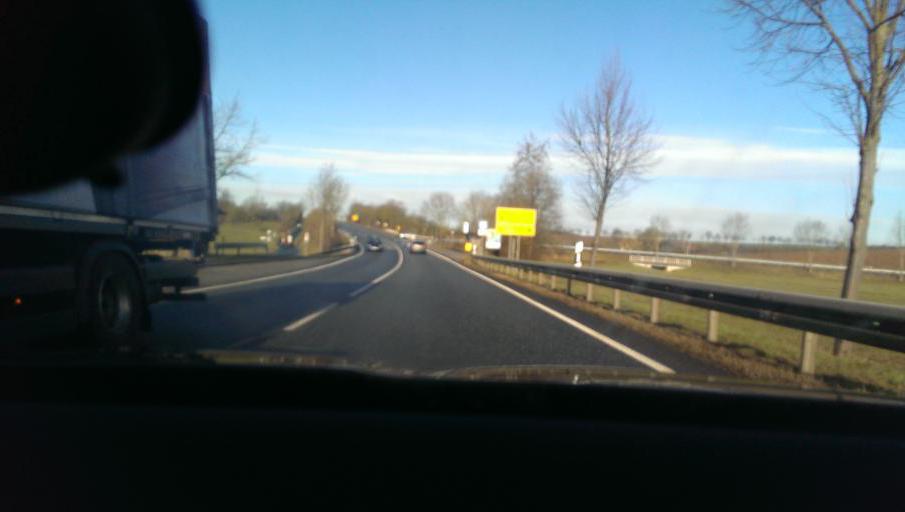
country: DE
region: Hesse
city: Hain-Grundau
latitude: 50.2360
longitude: 9.1298
